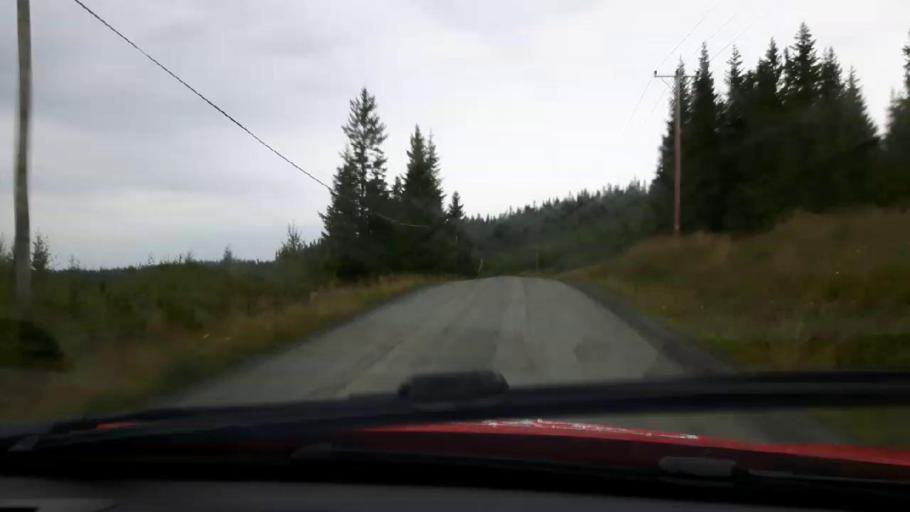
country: SE
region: Jaemtland
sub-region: Are Kommun
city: Are
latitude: 63.4158
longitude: 12.8265
